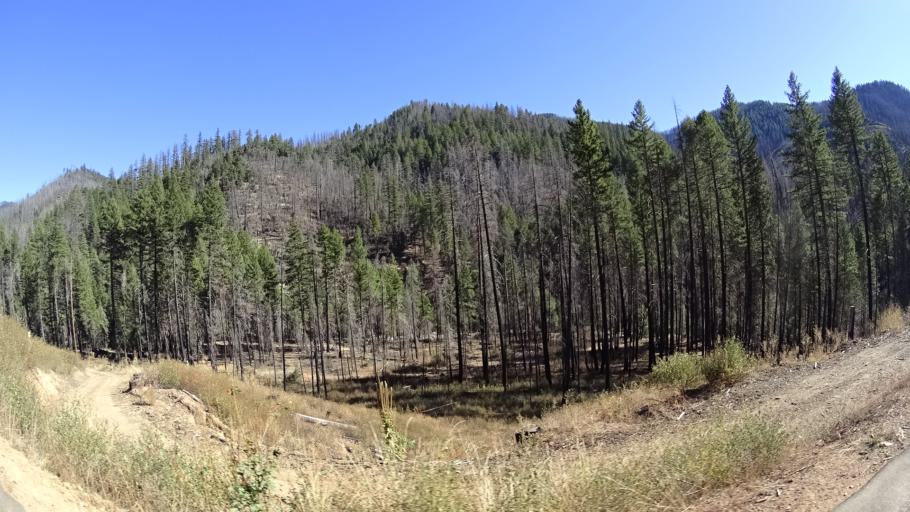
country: US
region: California
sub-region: Siskiyou County
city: Happy Camp
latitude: 41.3066
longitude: -123.0713
